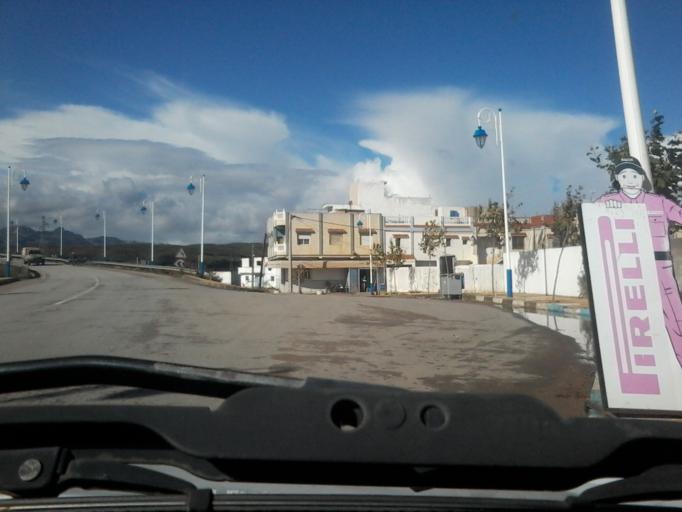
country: MA
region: Tanger-Tetouan
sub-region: Tetouan
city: Martil
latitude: 35.7021
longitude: -5.3508
